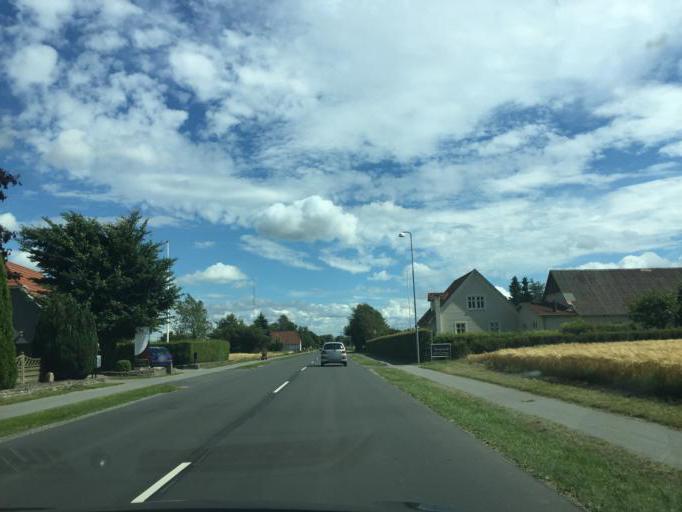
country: DK
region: South Denmark
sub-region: Nordfyns Kommune
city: Otterup
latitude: 55.5212
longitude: 10.3677
